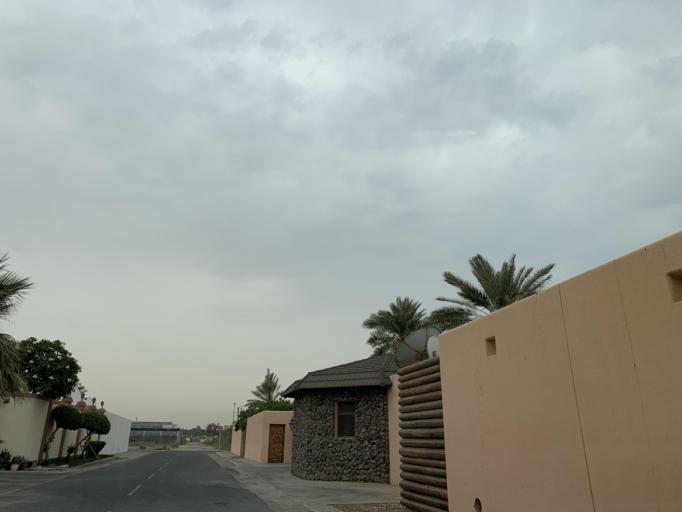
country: BH
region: Northern
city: Madinat `Isa
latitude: 26.1913
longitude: 50.4678
